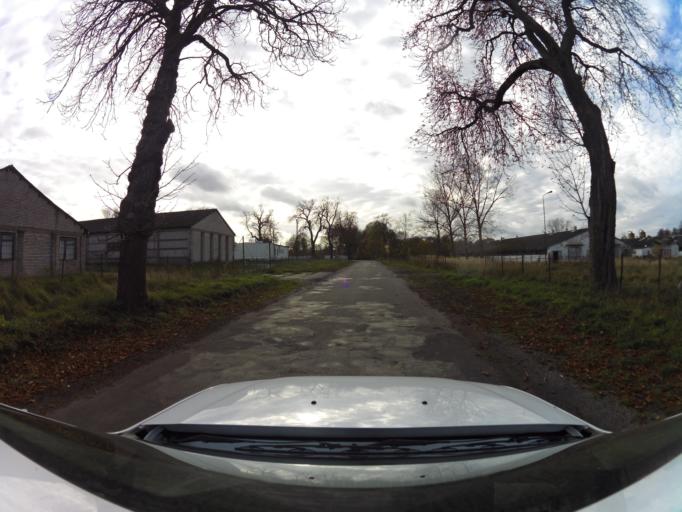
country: PL
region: West Pomeranian Voivodeship
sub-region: Powiat gryficki
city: Gryfice
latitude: 53.9555
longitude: 15.1897
